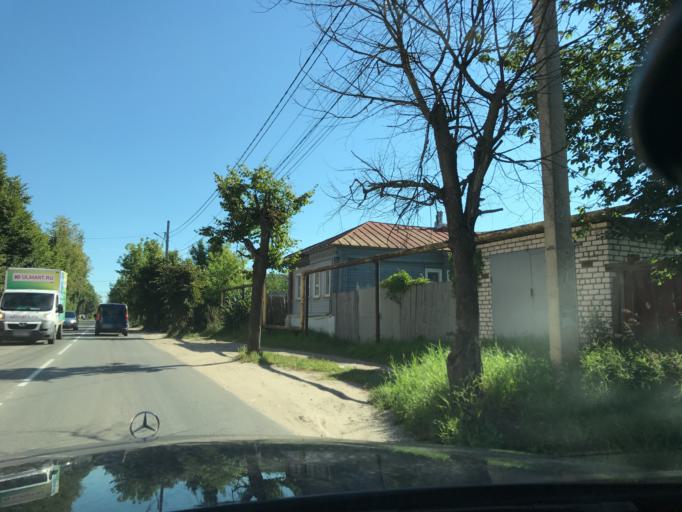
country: RU
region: Vladimir
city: Kirzhach
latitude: 56.1602
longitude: 38.8732
